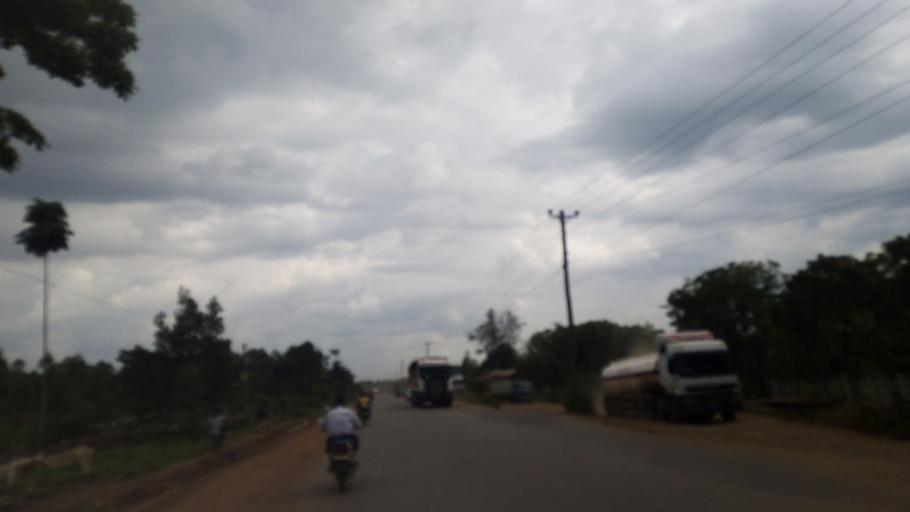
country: UG
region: Eastern Region
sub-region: Mbale District
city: Mbale
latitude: 1.0611
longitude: 34.1807
